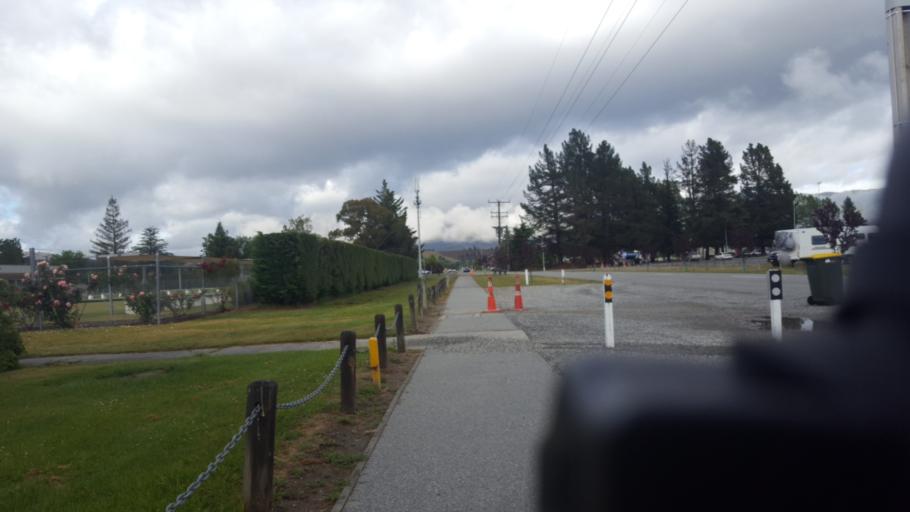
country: NZ
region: Otago
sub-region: Queenstown-Lakes District
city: Wanaka
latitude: -45.2433
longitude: 169.3813
